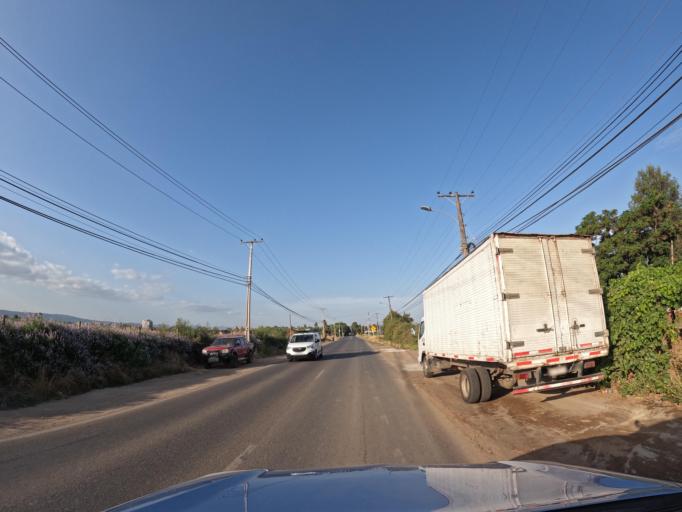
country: CL
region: Maule
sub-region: Provincia de Talca
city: Talca
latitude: -35.4470
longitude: -71.6174
